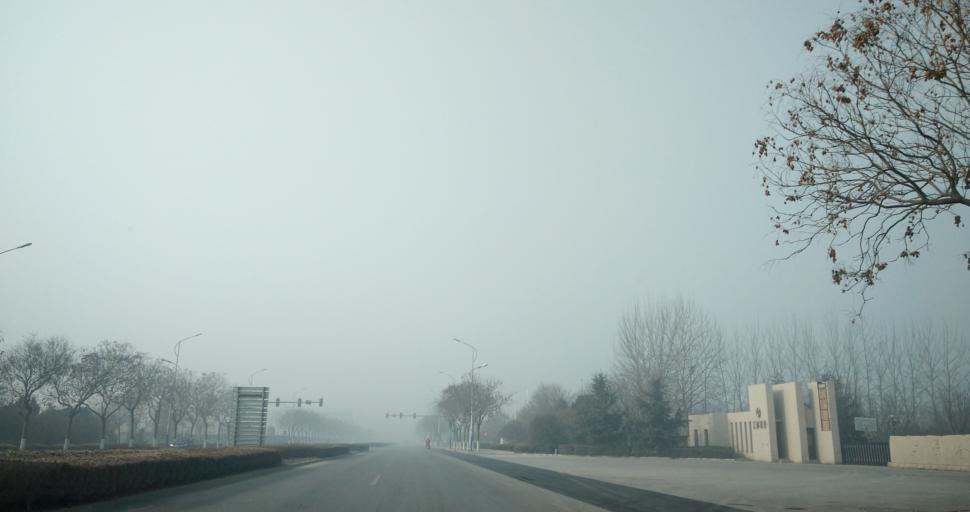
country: CN
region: Beijing
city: Yinghai
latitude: 39.7085
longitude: 116.4091
